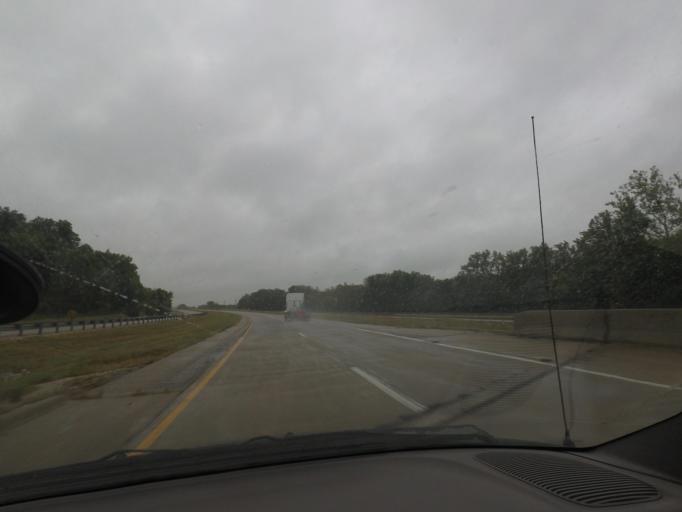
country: US
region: Illinois
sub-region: Pike County
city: Barry
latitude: 39.7126
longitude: -91.1007
